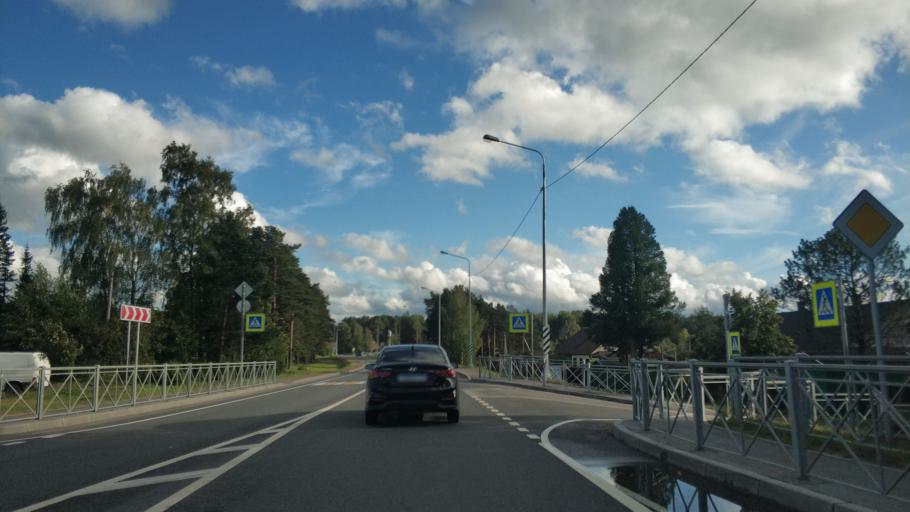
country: RU
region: Leningrad
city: Priozersk
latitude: 61.0017
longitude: 30.1813
